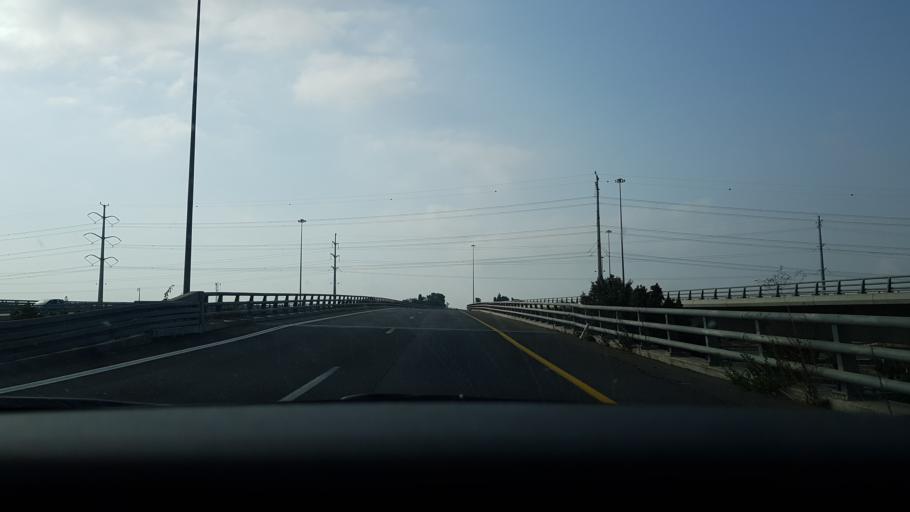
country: IL
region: Central District
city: Rishon LeZiyyon
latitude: 31.9547
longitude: 34.7847
